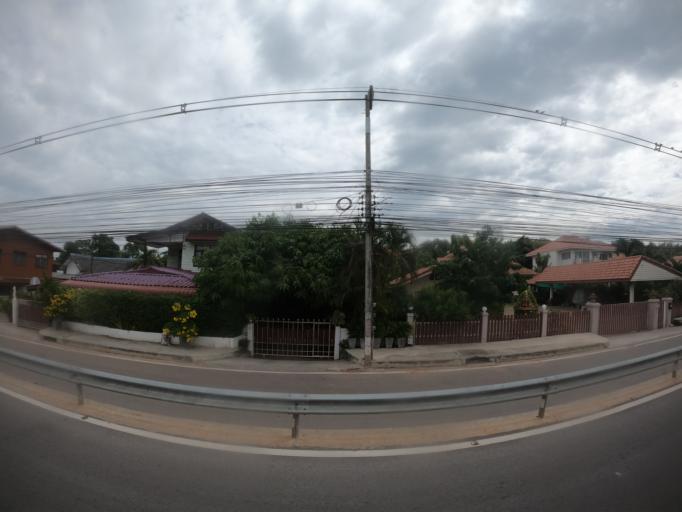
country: TH
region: Maha Sarakham
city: Kantharawichai
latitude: 16.3107
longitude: 103.3009
